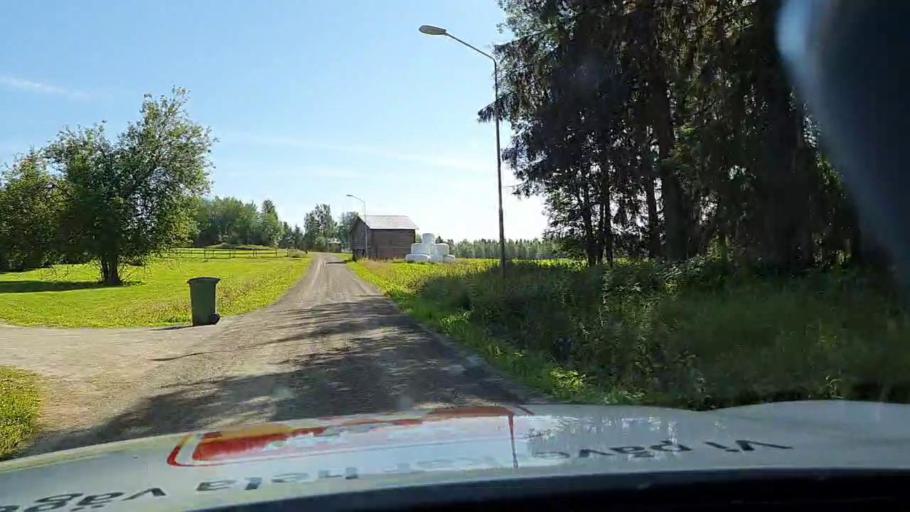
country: SE
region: Jaemtland
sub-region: Stroemsunds Kommun
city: Stroemsund
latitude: 63.7709
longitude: 15.3257
